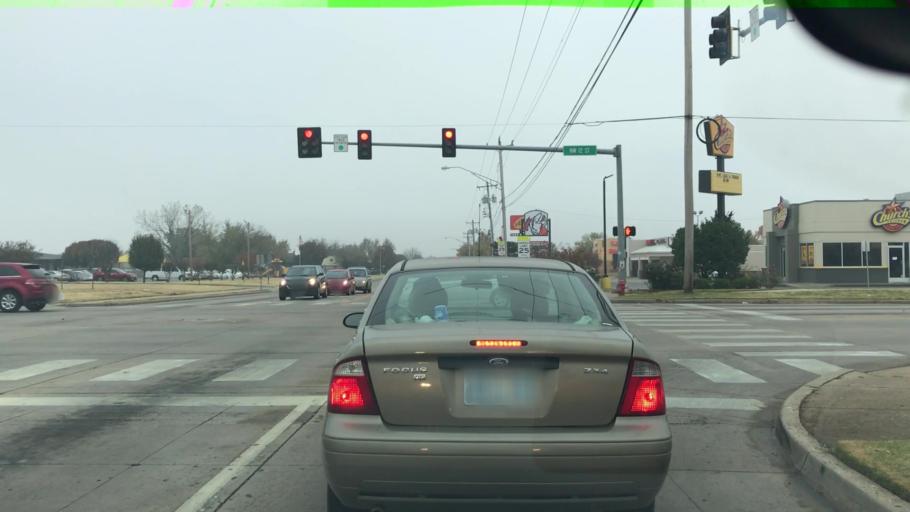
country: US
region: Oklahoma
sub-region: Cleveland County
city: Moore
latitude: 35.3491
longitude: -97.5122
